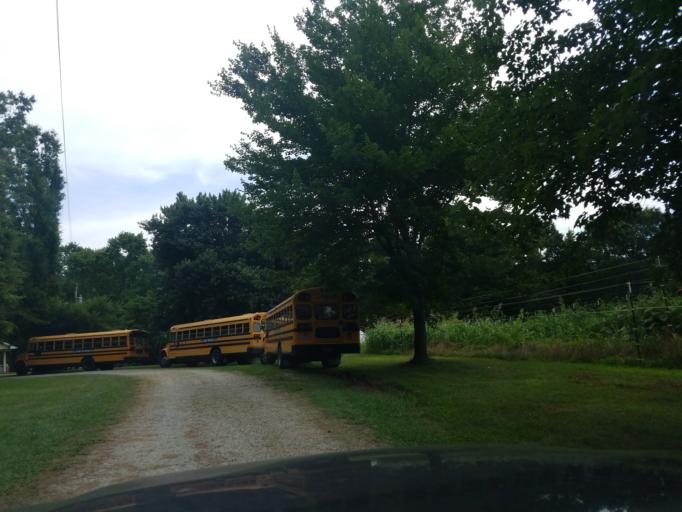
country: US
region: North Carolina
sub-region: Durham County
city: Durham
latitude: 36.1481
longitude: -78.9441
